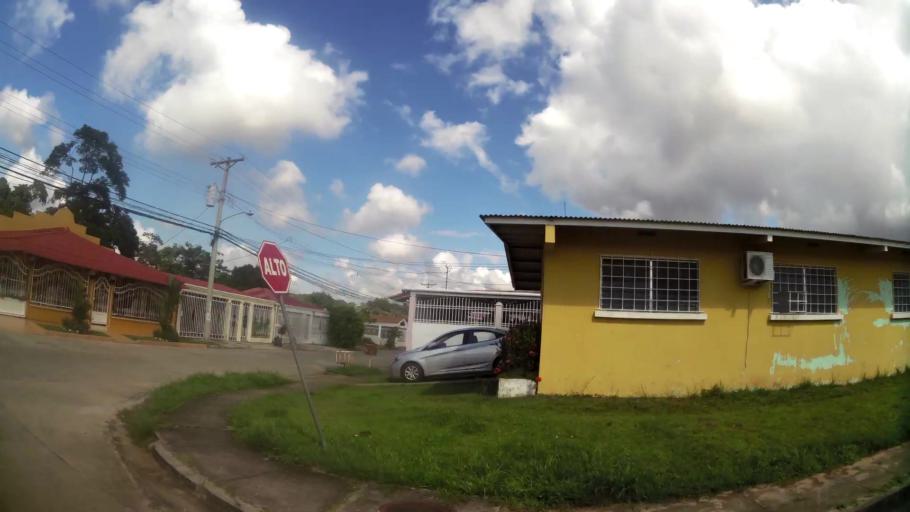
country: PA
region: Panama
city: Nuevo Arraijan
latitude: 8.9113
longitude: -79.7405
